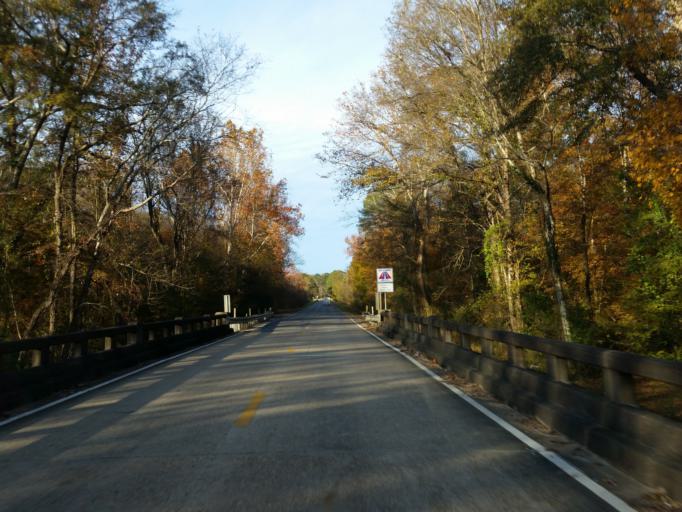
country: US
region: Mississippi
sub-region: Clarke County
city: Stonewall
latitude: 32.0635
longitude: -88.8801
